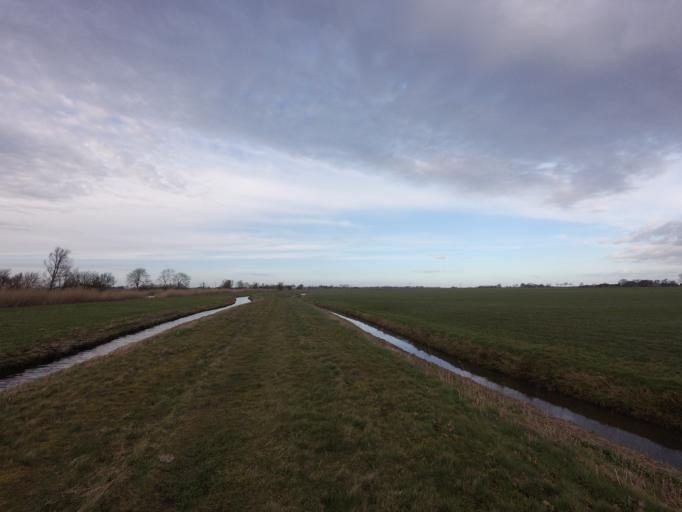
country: NL
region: Friesland
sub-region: Sudwest Fryslan
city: Bolsward
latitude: 53.0288
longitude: 5.4880
